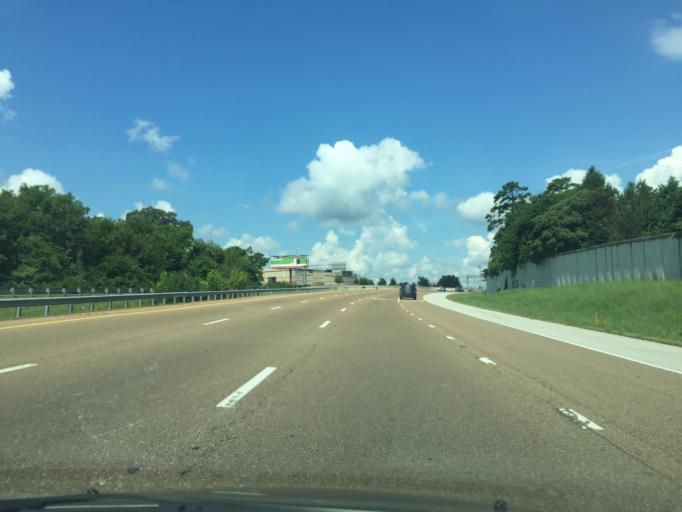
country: US
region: Tennessee
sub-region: Hamilton County
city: East Brainerd
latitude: 35.0290
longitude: -85.1773
